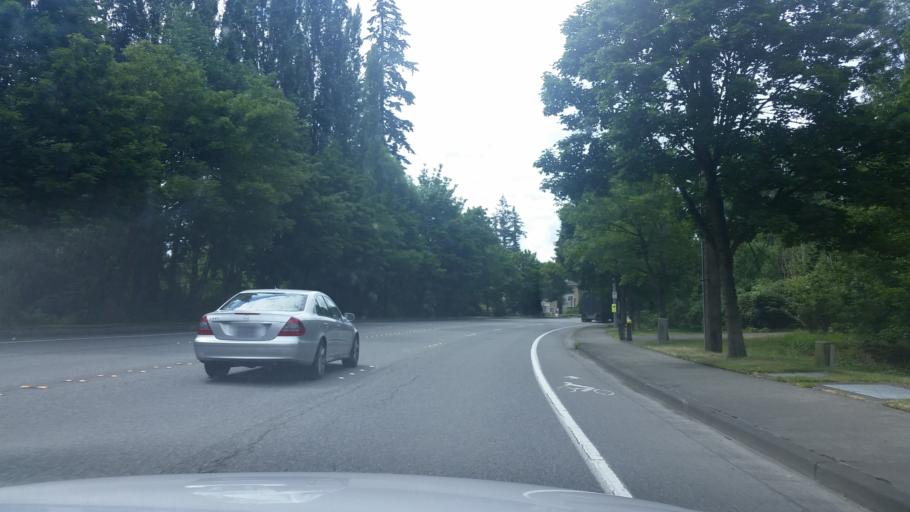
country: US
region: Washington
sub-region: King County
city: Redmond
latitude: 47.6904
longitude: -122.0919
